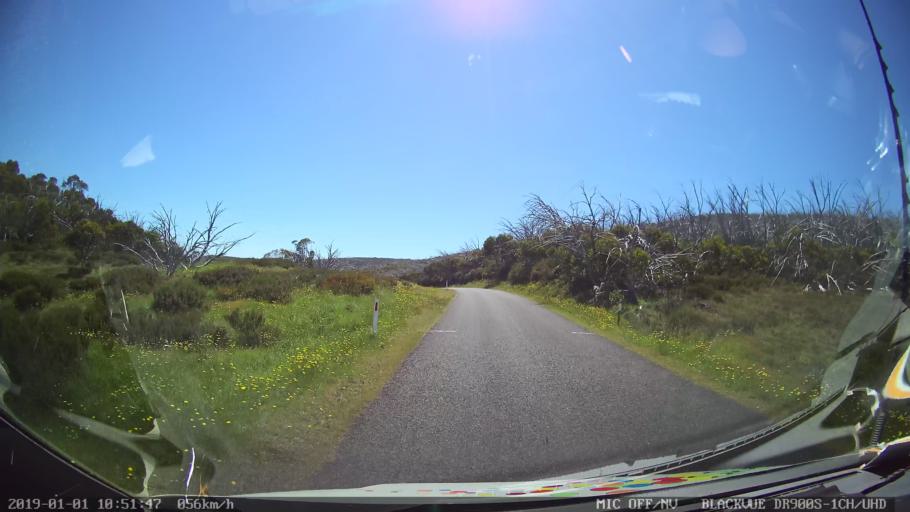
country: AU
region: New South Wales
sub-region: Snowy River
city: Jindabyne
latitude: -36.0193
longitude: 148.3750
